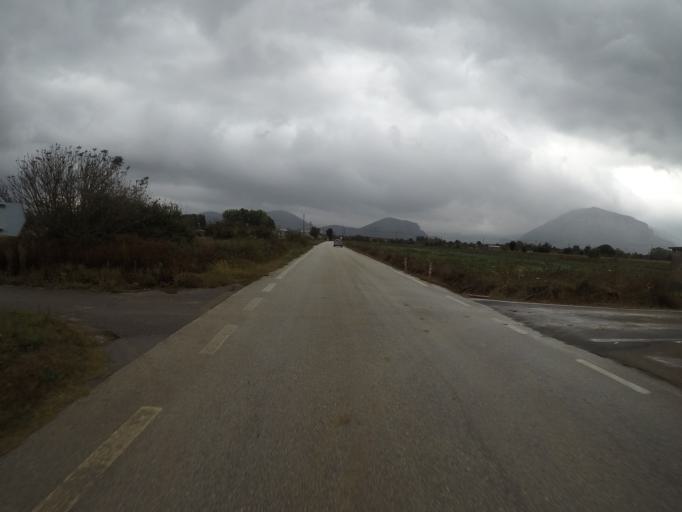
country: GR
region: Peloponnese
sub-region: Nomos Arkadias
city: Tripoli
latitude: 37.5700
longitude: 22.4099
